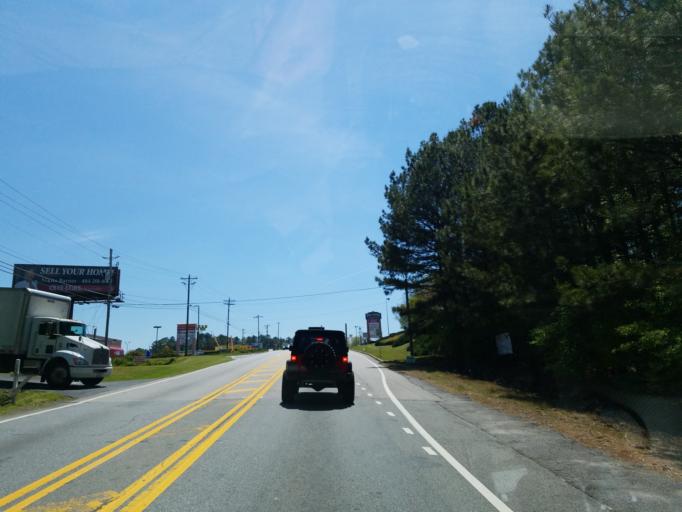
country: US
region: Georgia
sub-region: Paulding County
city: Hiram
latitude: 33.8940
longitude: -84.7538
